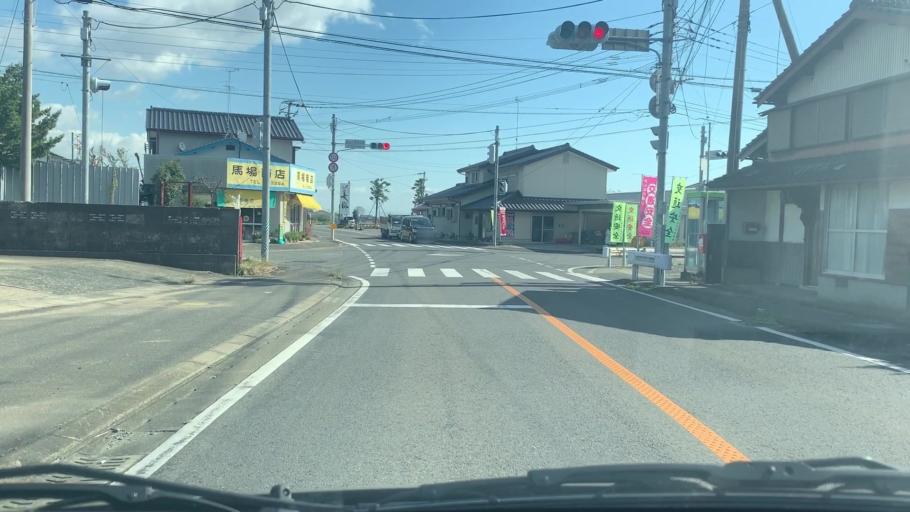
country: JP
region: Saga Prefecture
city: Saga-shi
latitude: 33.2719
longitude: 130.1875
